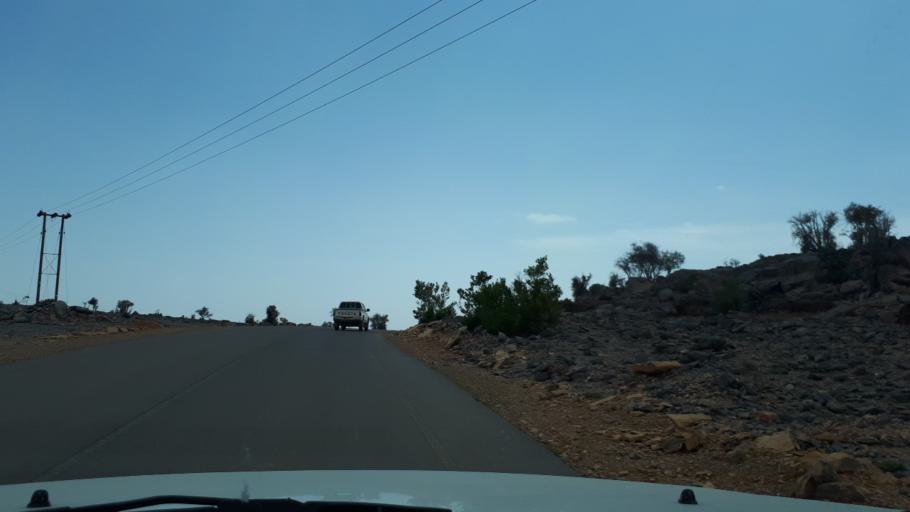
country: OM
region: Muhafazat ad Dakhiliyah
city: Bahla'
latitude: 23.2108
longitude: 57.2034
